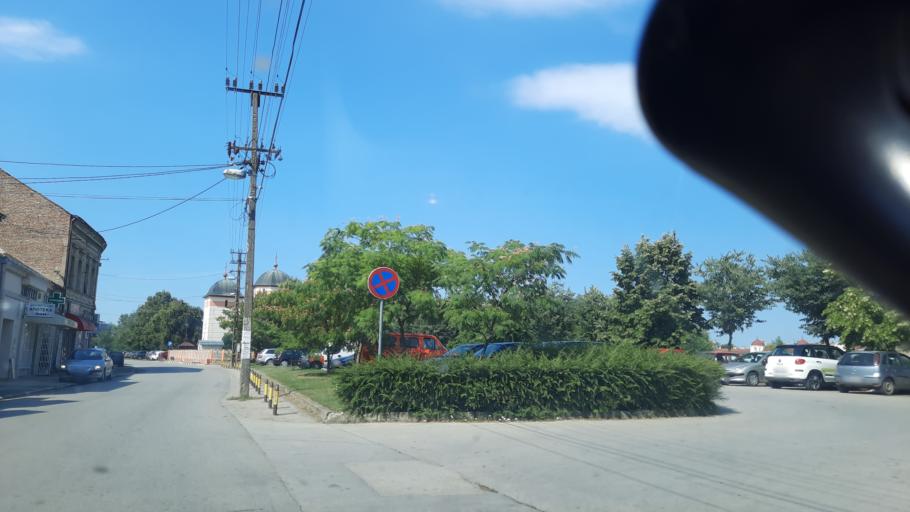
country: RS
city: Macvanska Mitrovica
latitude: 44.9654
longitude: 19.5992
